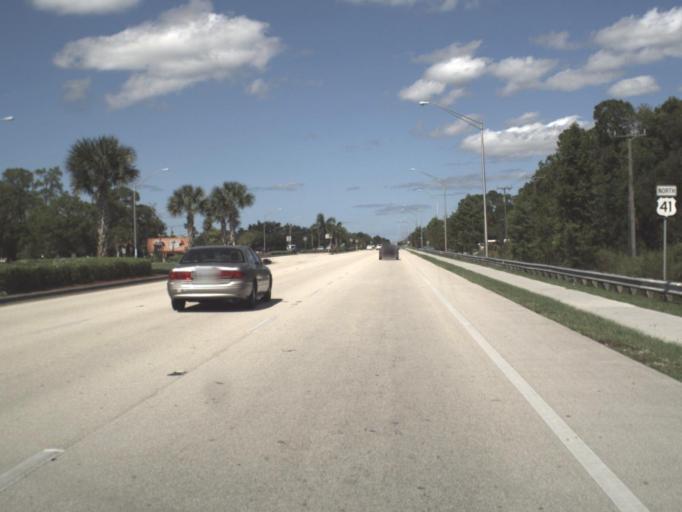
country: US
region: Florida
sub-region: Collier County
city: Naples Manor
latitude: 26.0869
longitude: -81.7293
